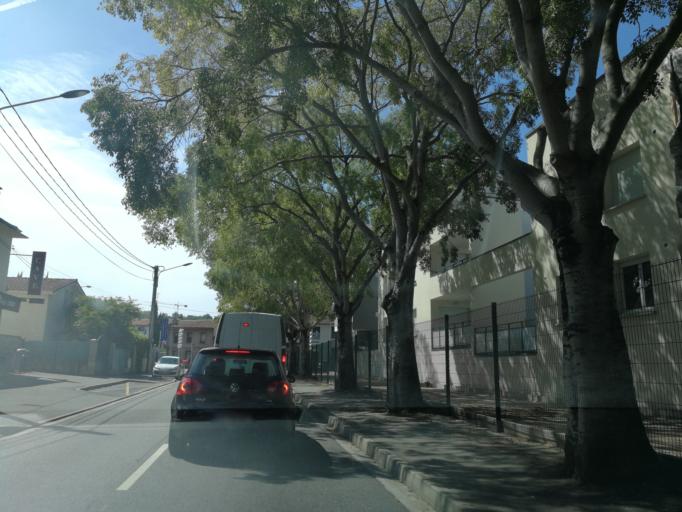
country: FR
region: Midi-Pyrenees
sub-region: Departement de la Haute-Garonne
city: Toulouse
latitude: 43.5748
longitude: 1.4526
